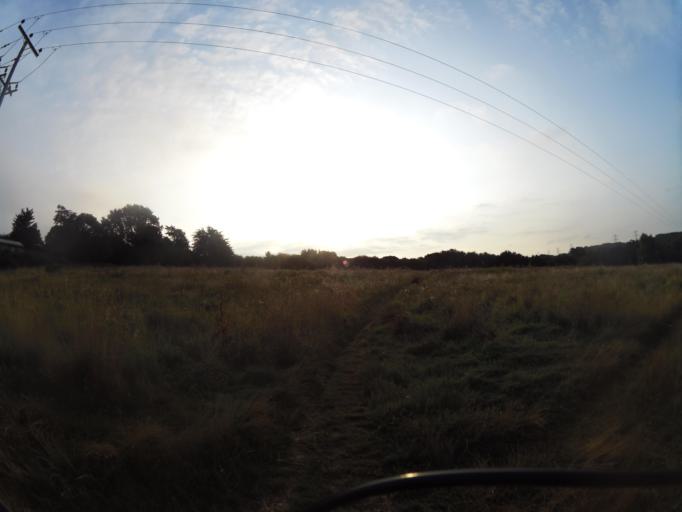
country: GB
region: England
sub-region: Suffolk
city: Bramford
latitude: 52.0364
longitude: 1.1033
